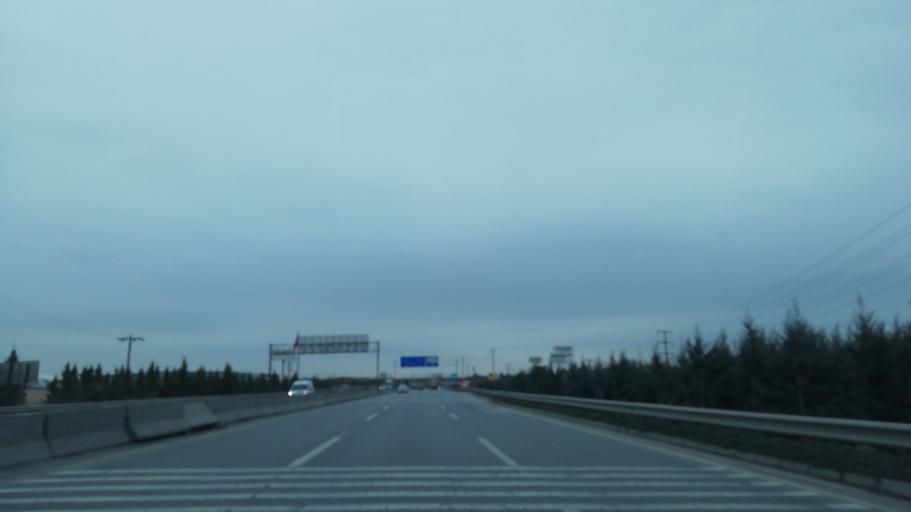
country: TR
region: Kocaeli
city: Tavsanli
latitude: 40.8030
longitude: 29.4772
